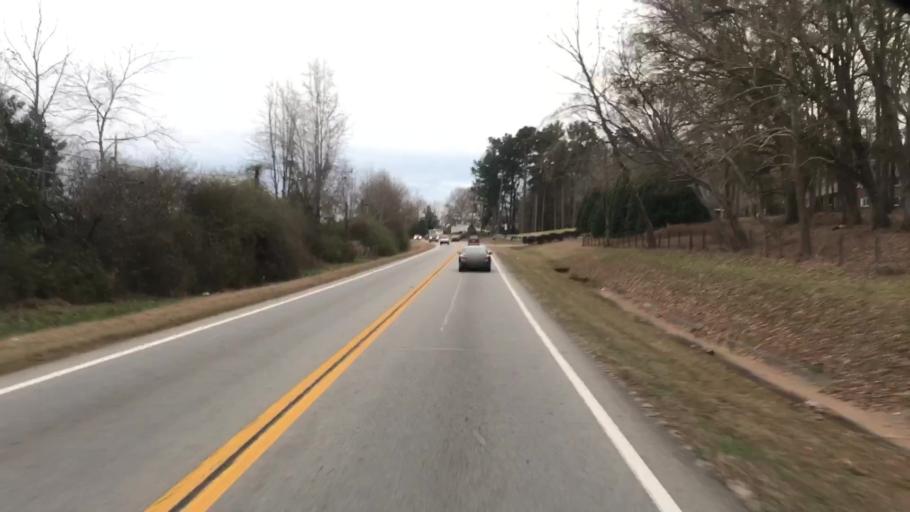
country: US
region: Georgia
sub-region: Barrow County
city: Auburn
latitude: 34.0254
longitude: -83.7703
